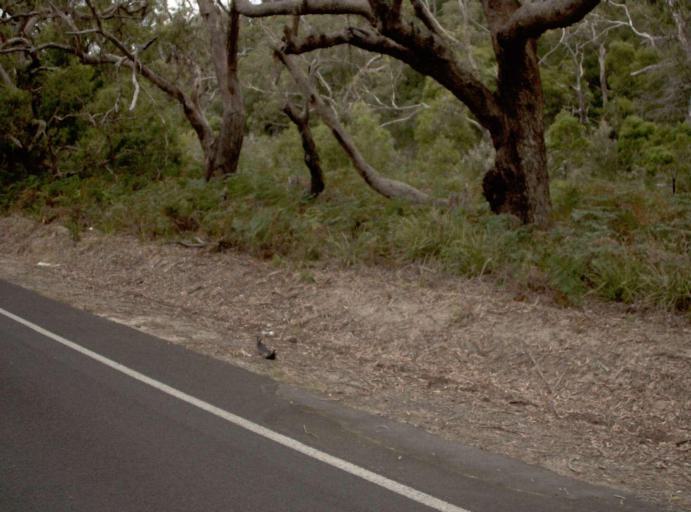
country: AU
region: Victoria
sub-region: Wellington
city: Sale
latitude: -38.2150
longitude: 147.0618
